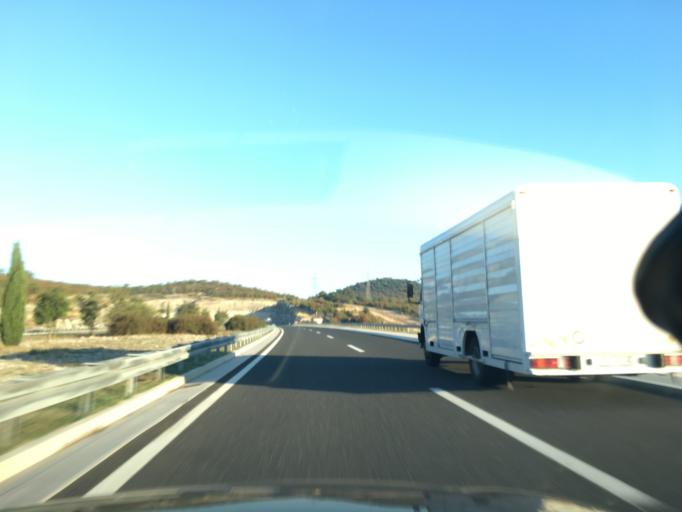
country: HR
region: Splitsko-Dalmatinska
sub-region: Grad Trogir
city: Trogir
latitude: 43.6538
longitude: 16.1970
